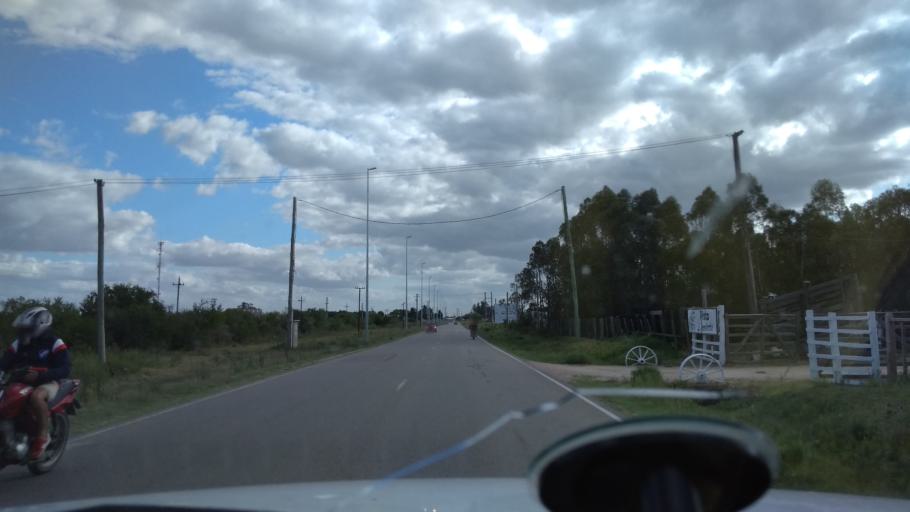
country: UY
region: Canelones
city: Tala
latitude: -34.1882
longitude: -55.7246
